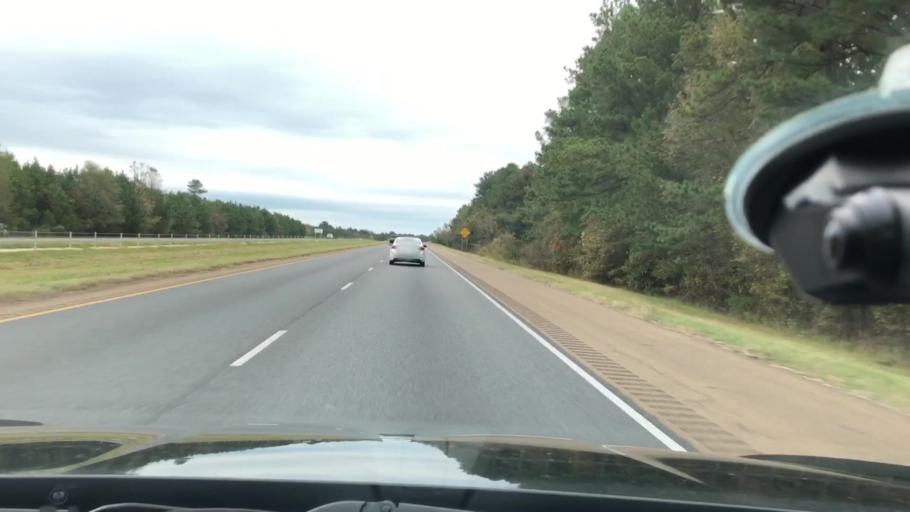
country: US
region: Arkansas
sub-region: Clark County
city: Gurdon
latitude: 33.9481
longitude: -93.2365
